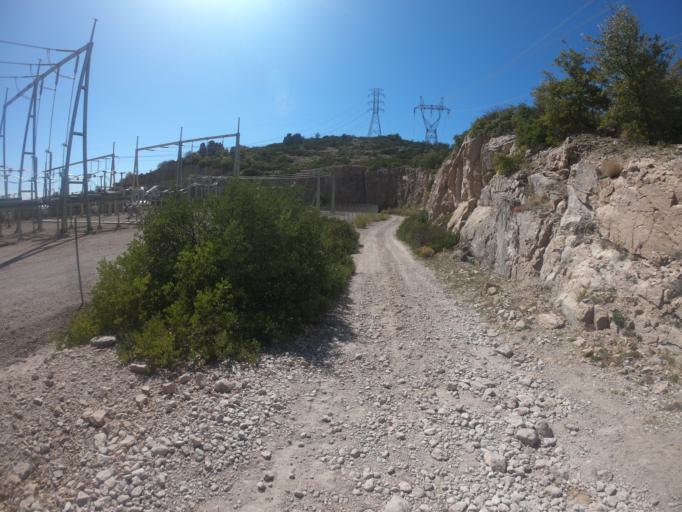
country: US
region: Arizona
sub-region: Pinal County
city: Superior
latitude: 33.3397
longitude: -111.0399
